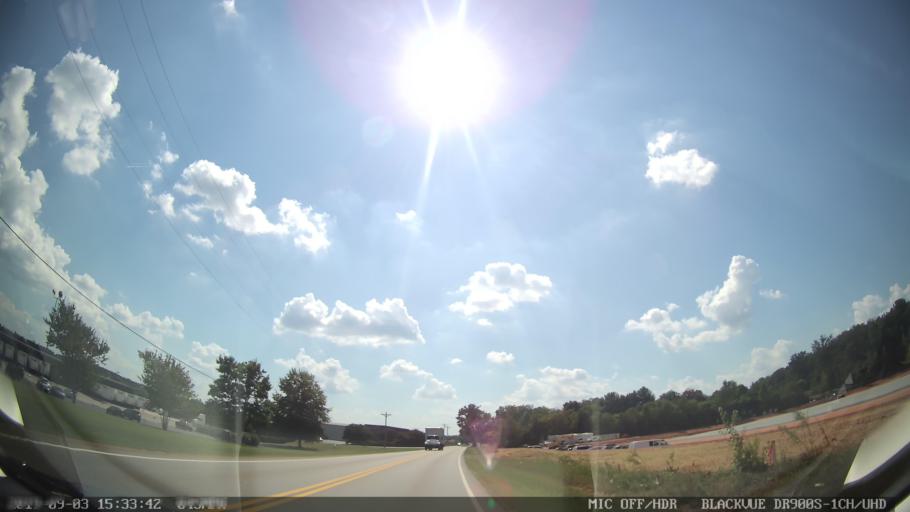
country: US
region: South Carolina
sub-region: Spartanburg County
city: Duncan
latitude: 34.8787
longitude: -82.1324
